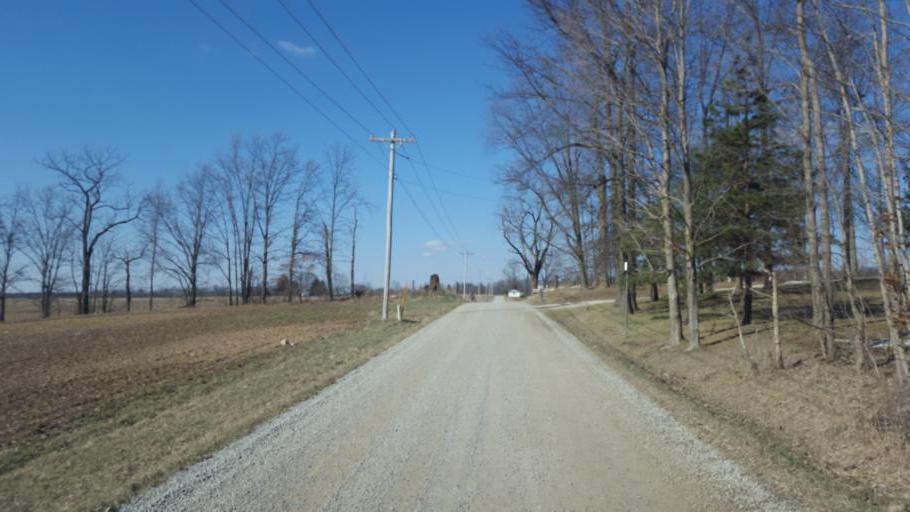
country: US
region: Ohio
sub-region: Morrow County
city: Mount Gilead
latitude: 40.5019
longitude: -82.7718
